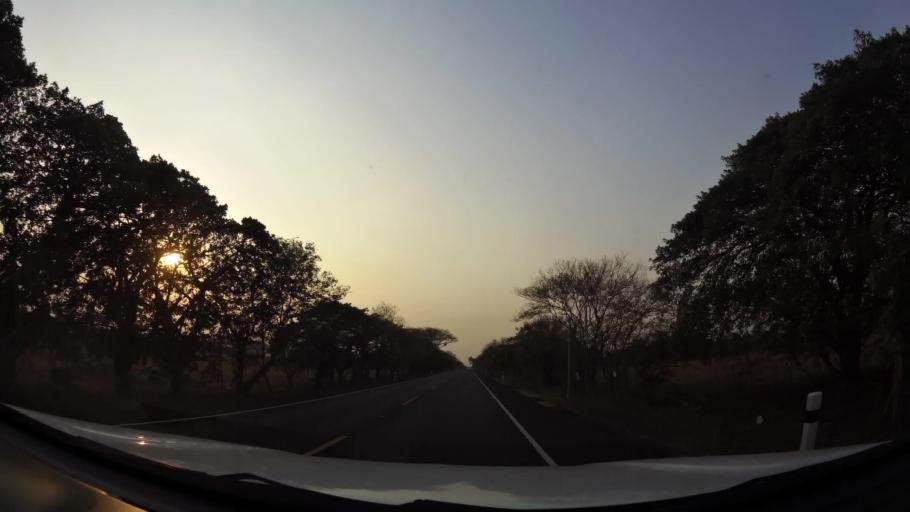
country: NI
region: Leon
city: Nagarote
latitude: 12.2981
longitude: -86.5940
